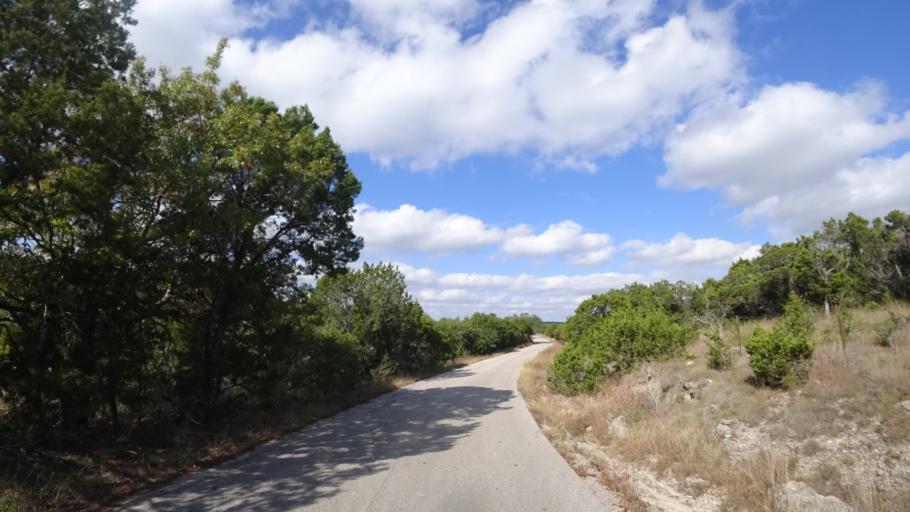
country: US
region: Texas
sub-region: Travis County
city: Bee Cave
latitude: 30.2571
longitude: -97.9408
